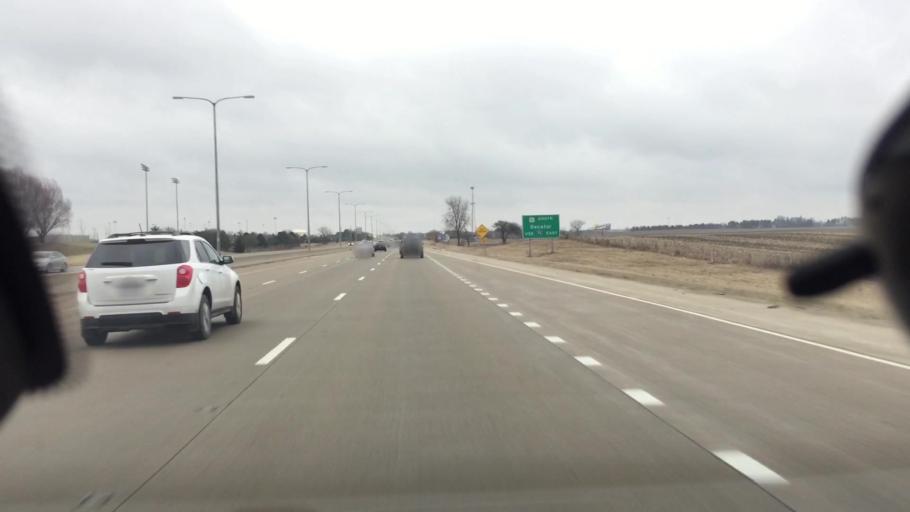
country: US
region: Illinois
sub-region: McLean County
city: Normal
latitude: 40.5269
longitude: -89.0283
